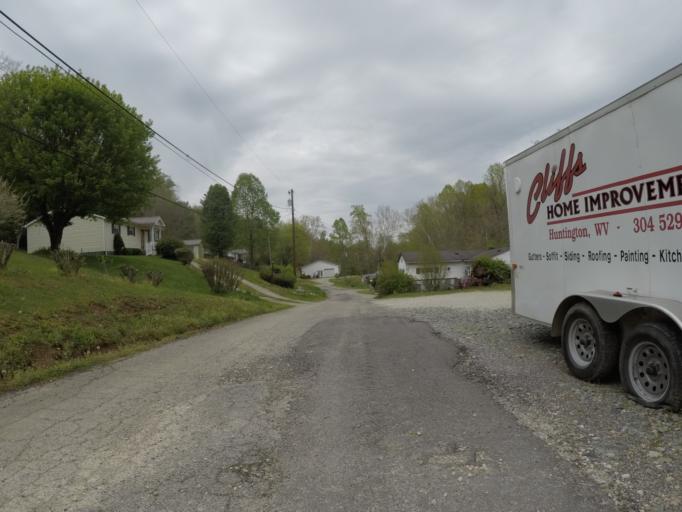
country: US
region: West Virginia
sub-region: Cabell County
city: Huntington
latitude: 38.3886
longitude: -82.4856
